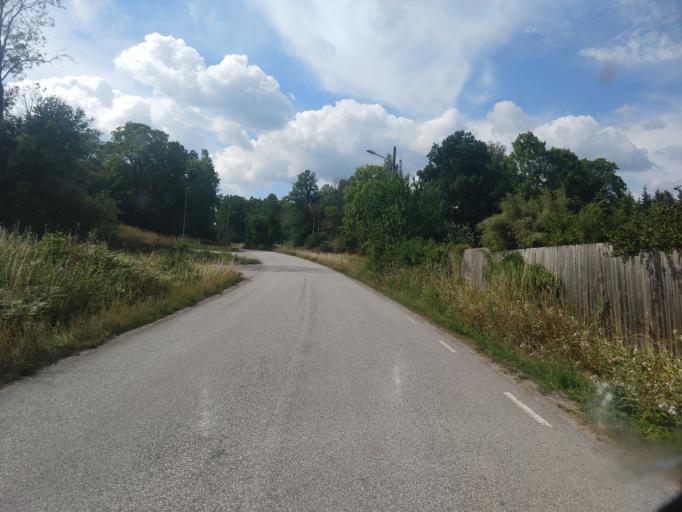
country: SE
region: Blekinge
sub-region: Karlskrona Kommun
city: Rodeby
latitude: 56.2288
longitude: 15.5846
